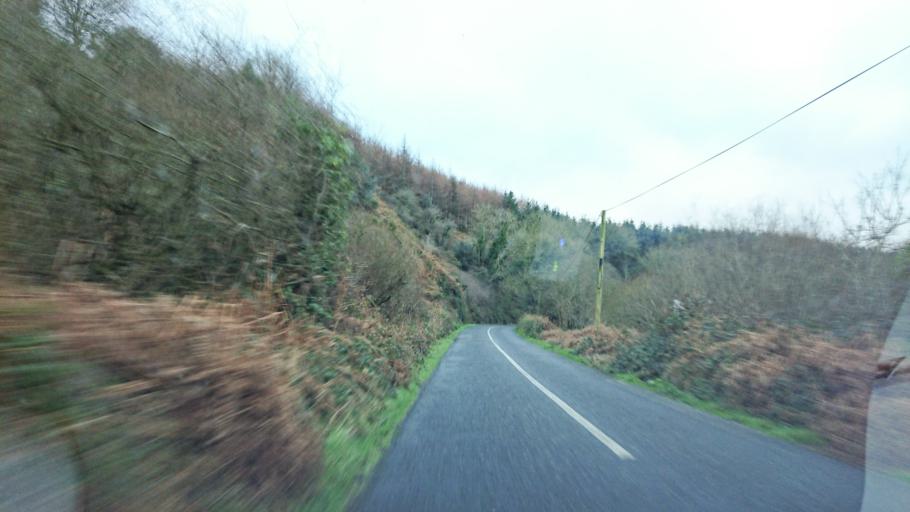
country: IE
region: Munster
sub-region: Waterford
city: Portlaw
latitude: 52.2134
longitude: -7.4193
